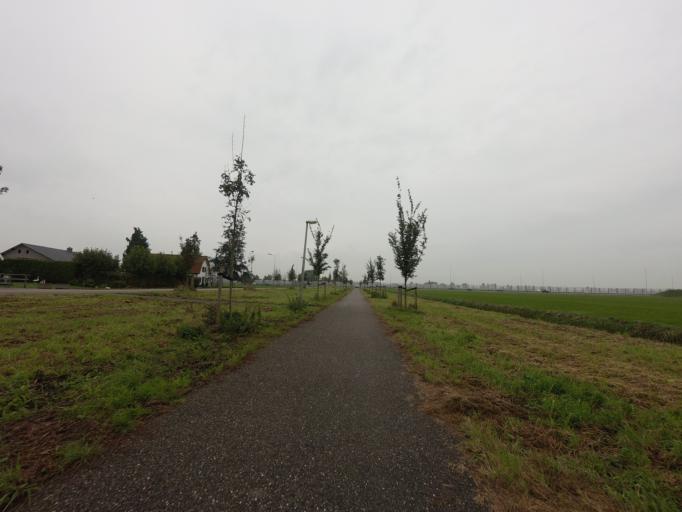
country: NL
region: Utrecht
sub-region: Gemeente Vianen
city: Vianen
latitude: 51.9475
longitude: 5.1427
